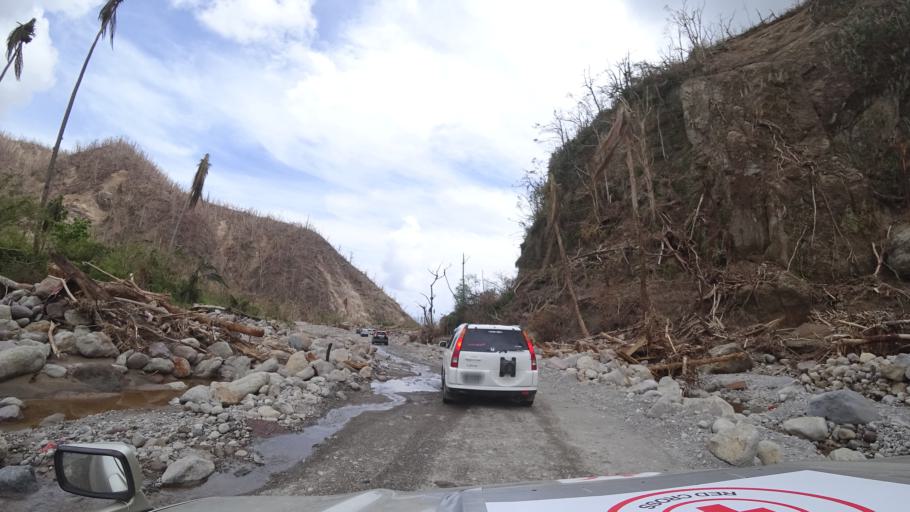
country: DM
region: Saint Patrick
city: Berekua
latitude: 15.2551
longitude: -61.3180
